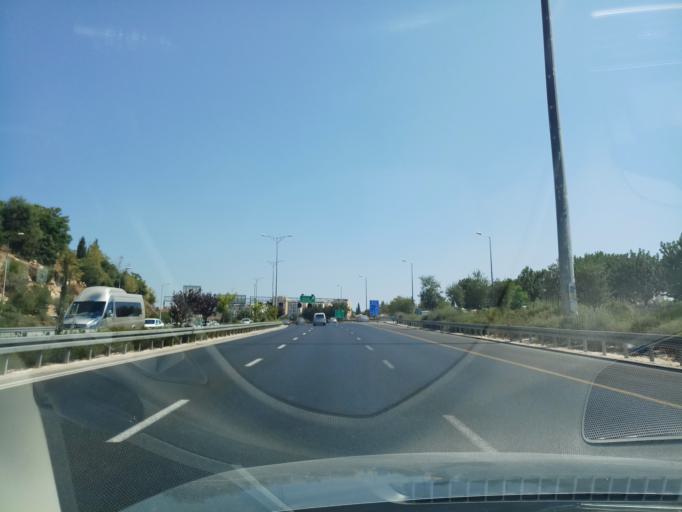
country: IL
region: Jerusalem
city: Jerusalem
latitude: 31.7585
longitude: 35.1931
